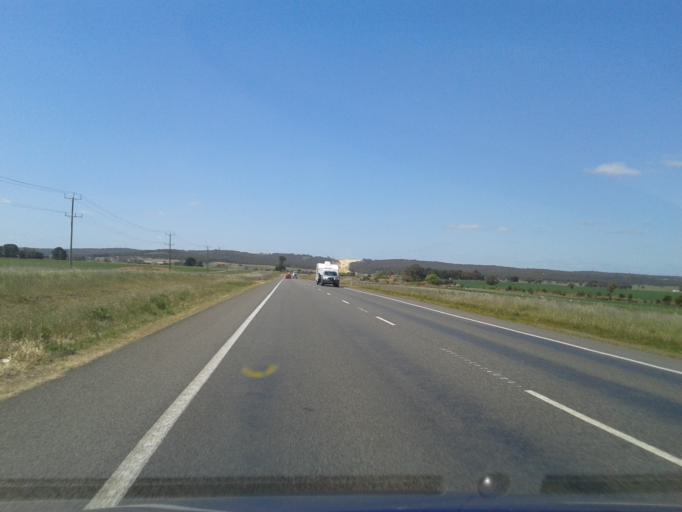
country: AU
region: Victoria
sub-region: Ararat
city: Ararat
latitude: -37.4002
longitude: 143.2922
